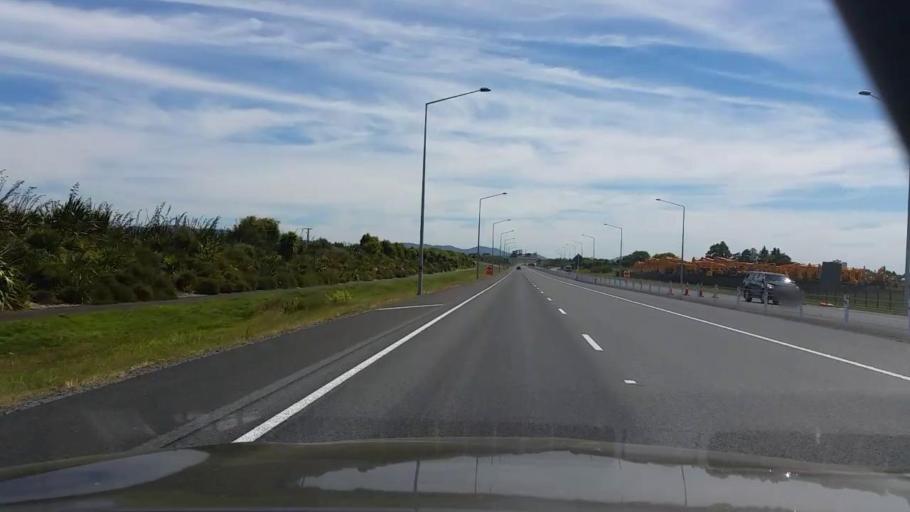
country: NZ
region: Waikato
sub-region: Hamilton City
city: Hamilton
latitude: -37.7406
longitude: 175.2128
